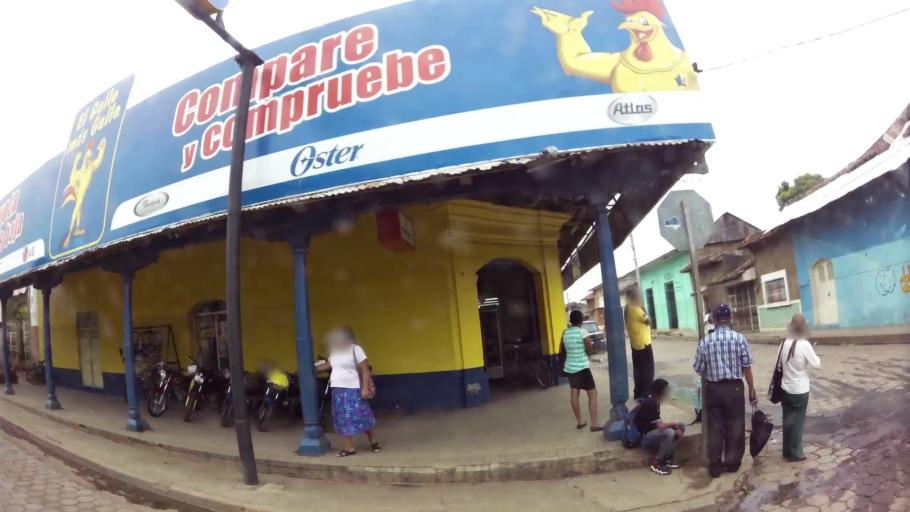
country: NI
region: Granada
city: Nandaime
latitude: 11.7569
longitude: -86.0526
